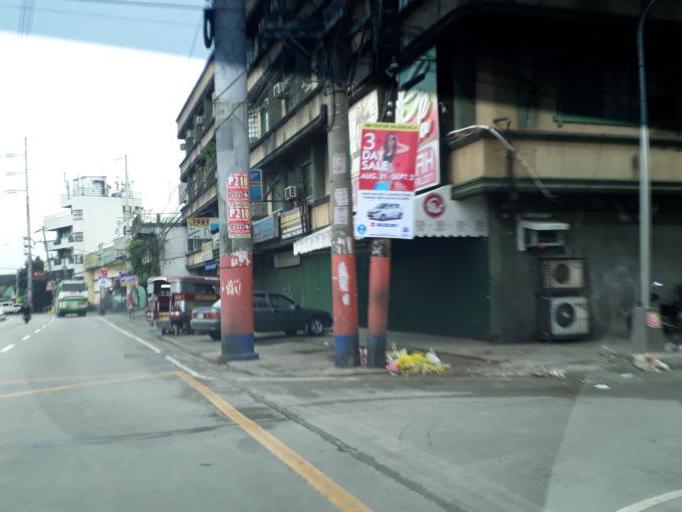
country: PH
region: Metro Manila
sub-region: Caloocan City
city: Niugan
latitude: 14.6646
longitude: 120.9843
